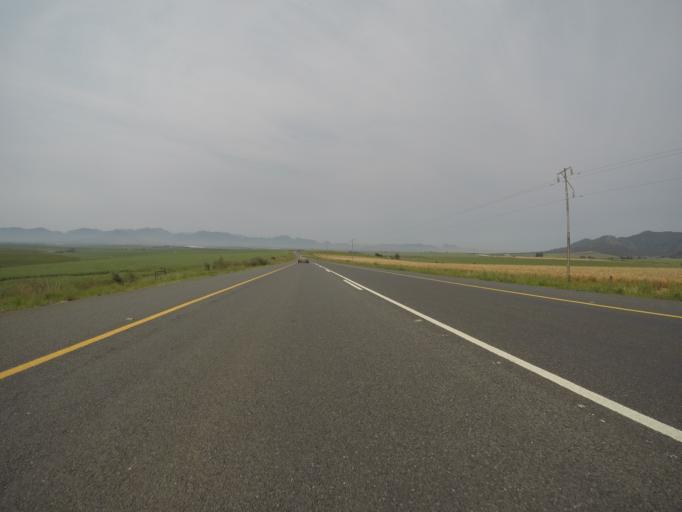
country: ZA
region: Western Cape
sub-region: West Coast District Municipality
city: Malmesbury
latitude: -33.5401
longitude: 18.8582
